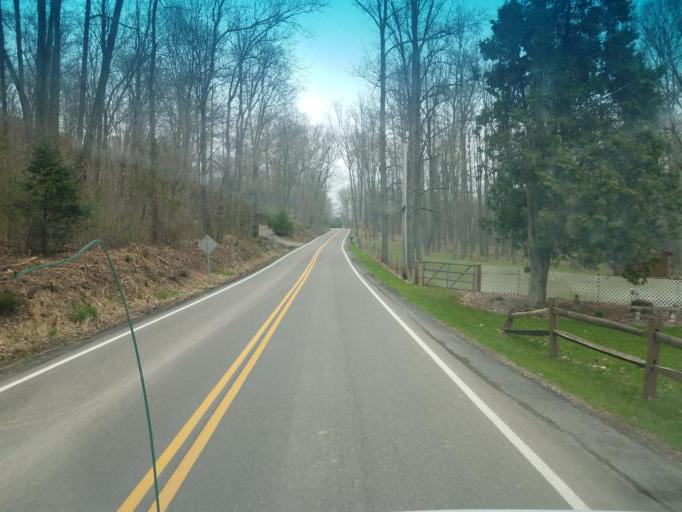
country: US
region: Ohio
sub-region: Stark County
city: Beach City
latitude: 40.6058
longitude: -81.6717
